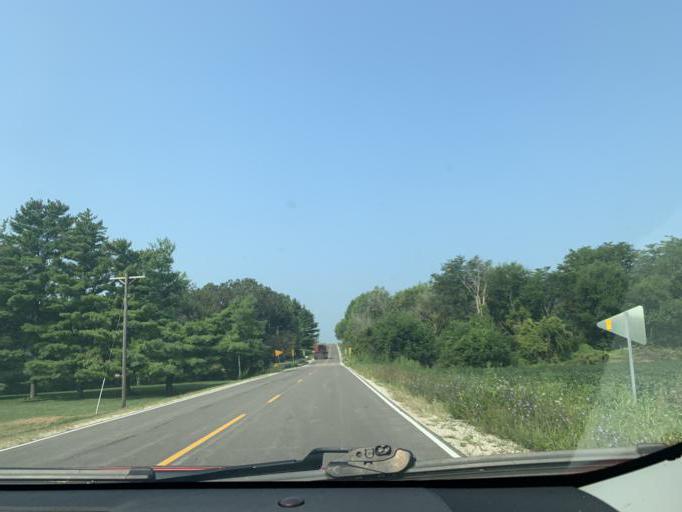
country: US
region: Illinois
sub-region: Whiteside County
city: Sterling
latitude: 41.8441
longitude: -89.7812
